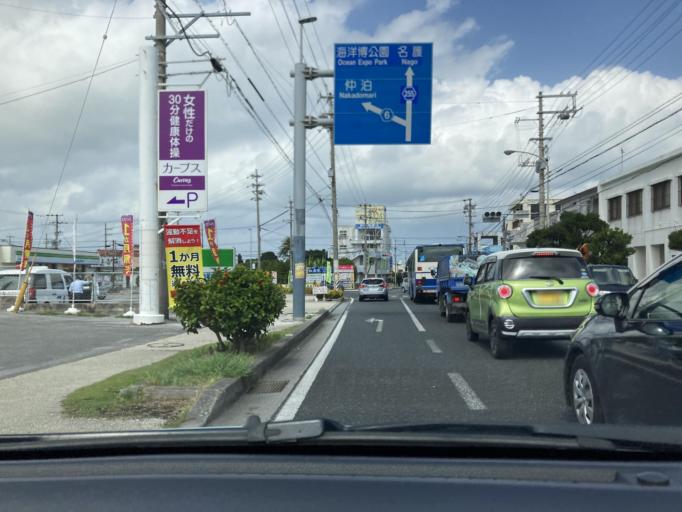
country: JP
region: Okinawa
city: Ishikawa
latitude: 26.4105
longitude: 127.8276
